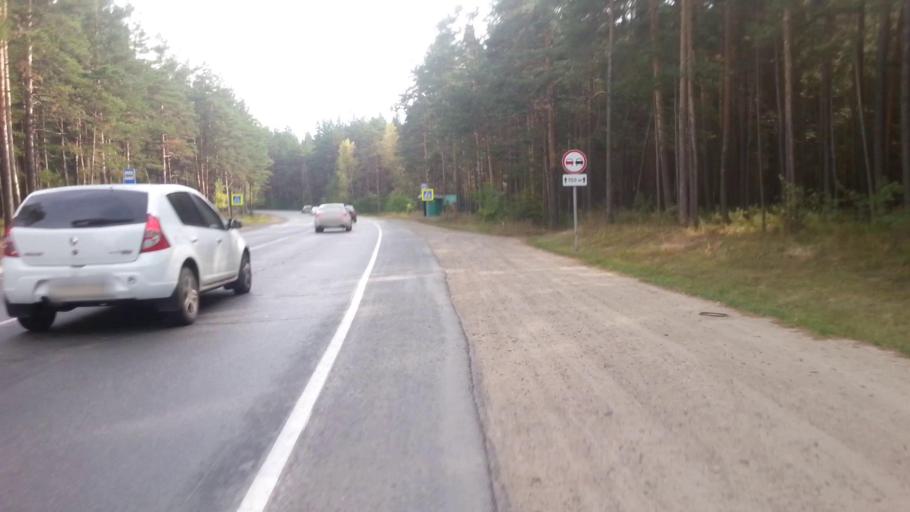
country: RU
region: Altai Krai
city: Yuzhnyy
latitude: 53.2998
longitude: 83.7029
